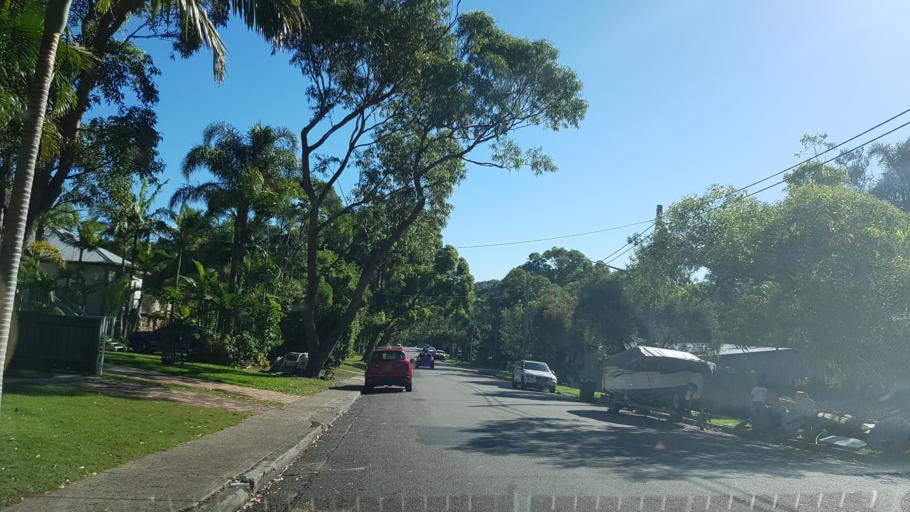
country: AU
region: New South Wales
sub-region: Pittwater
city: Bilgola Beach
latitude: -33.6231
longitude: 151.3368
